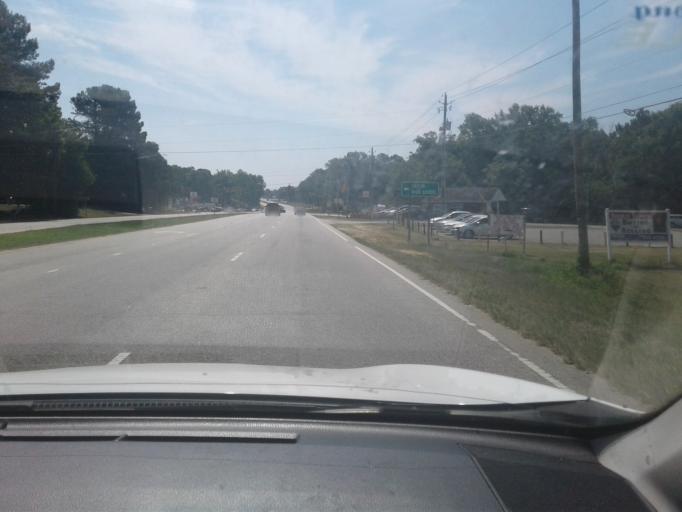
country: US
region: North Carolina
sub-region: Harnett County
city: Erwin
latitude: 35.3360
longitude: -78.6750
